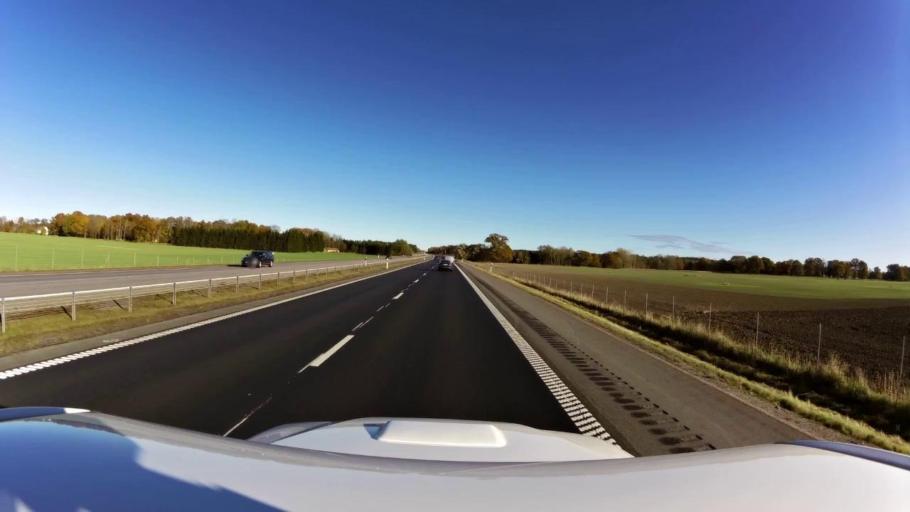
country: SE
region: OEstergoetland
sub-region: Linkopings Kommun
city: Vikingstad
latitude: 58.4112
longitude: 15.4638
